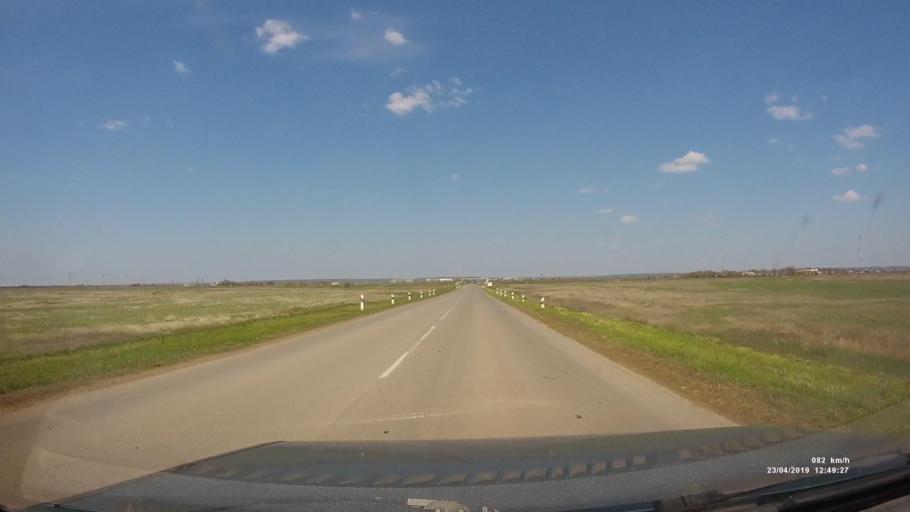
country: RU
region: Kalmykiya
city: Yashalta
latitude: 46.5373
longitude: 42.6394
